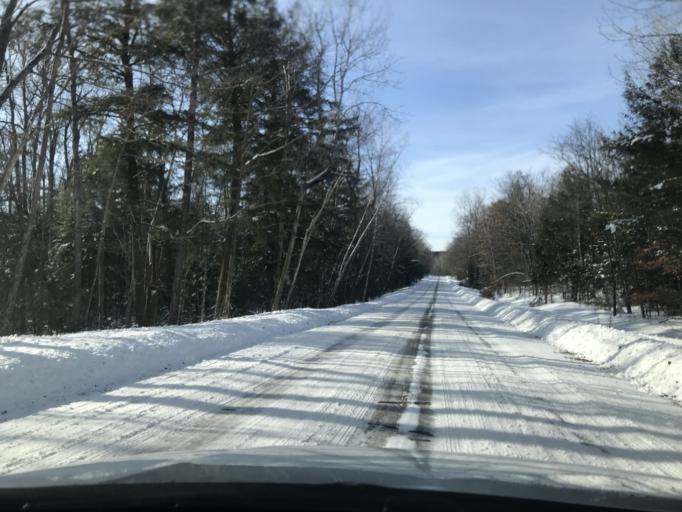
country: US
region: Wisconsin
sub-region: Oconto County
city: Gillett
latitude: 45.1572
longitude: -88.2036
